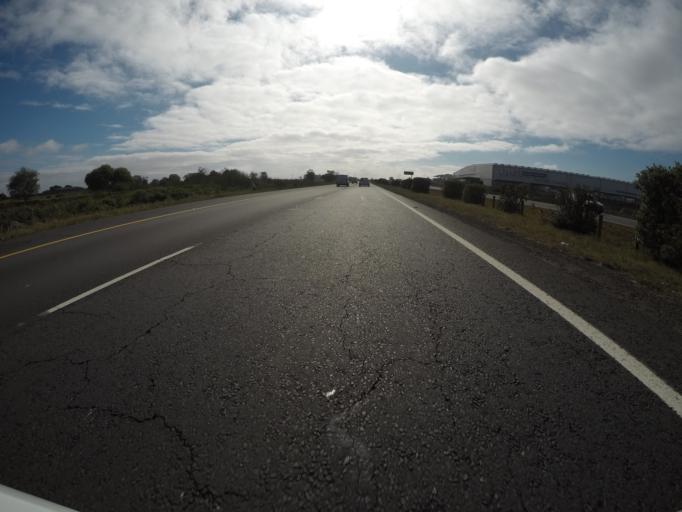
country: ZA
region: Western Cape
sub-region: City of Cape Town
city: Kraaifontein
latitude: -33.8328
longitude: 18.7450
